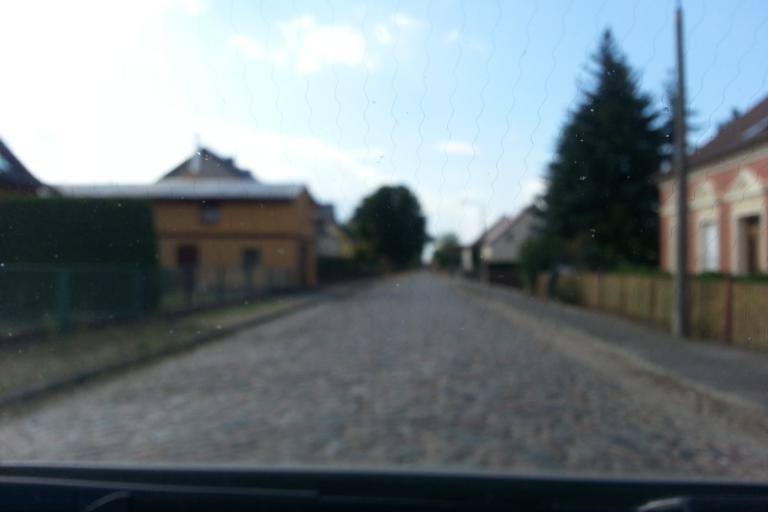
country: DE
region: Mecklenburg-Vorpommern
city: Ferdinandshof
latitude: 53.6322
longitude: 13.8559
